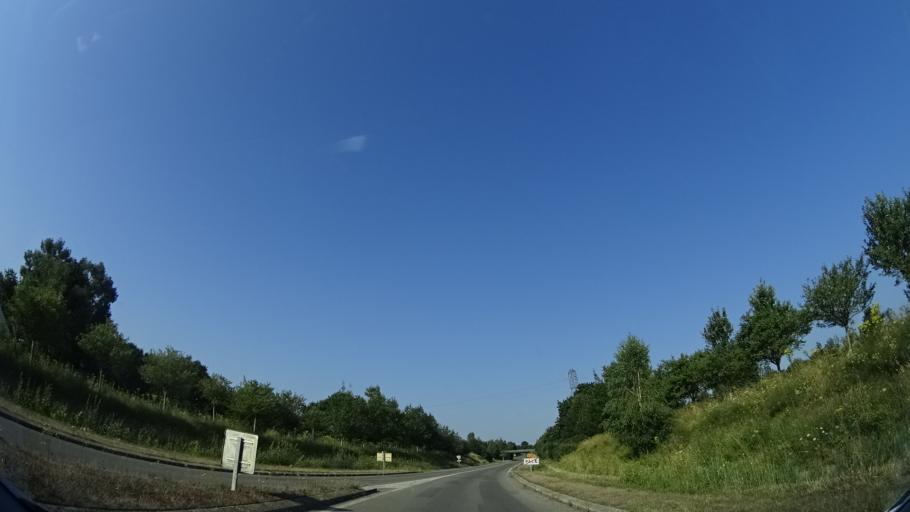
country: FR
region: Brittany
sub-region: Departement d'Ille-et-Vilaine
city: Pace
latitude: 48.1520
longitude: -1.7929
